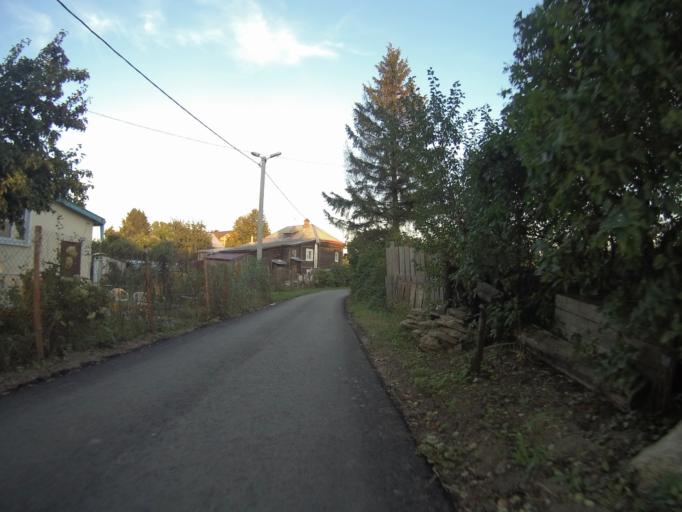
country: RU
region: Vladimir
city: Vladimir
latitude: 56.1167
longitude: 40.3853
